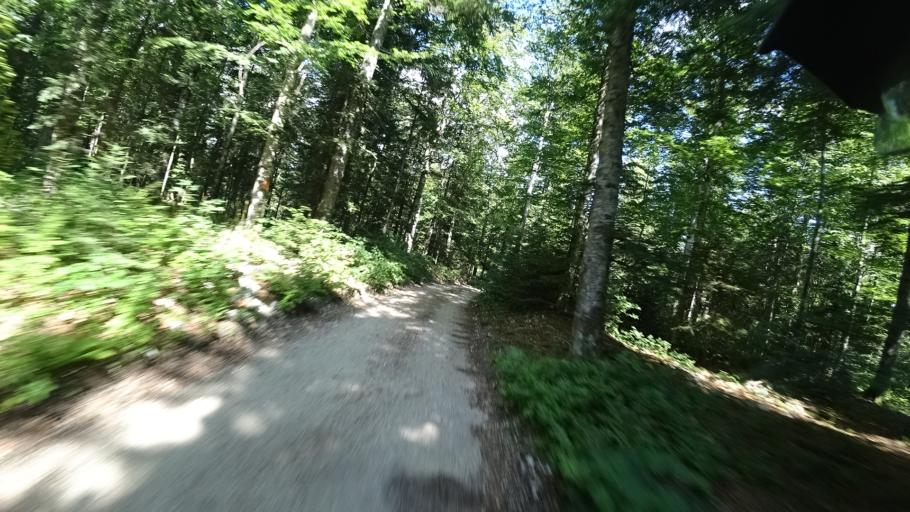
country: BA
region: Federation of Bosnia and Herzegovina
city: Orasac
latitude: 44.5003
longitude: 15.9366
